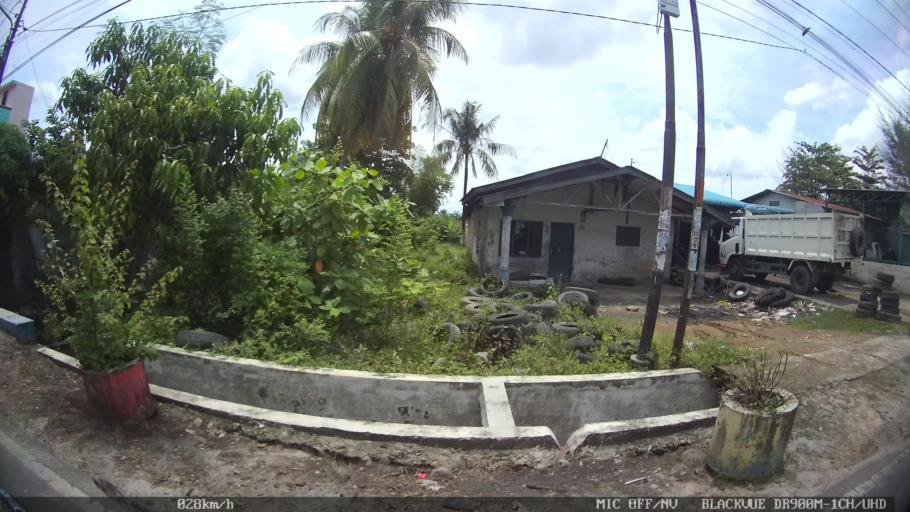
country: ID
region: North Sumatra
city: Percut
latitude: 3.5648
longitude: 98.8830
